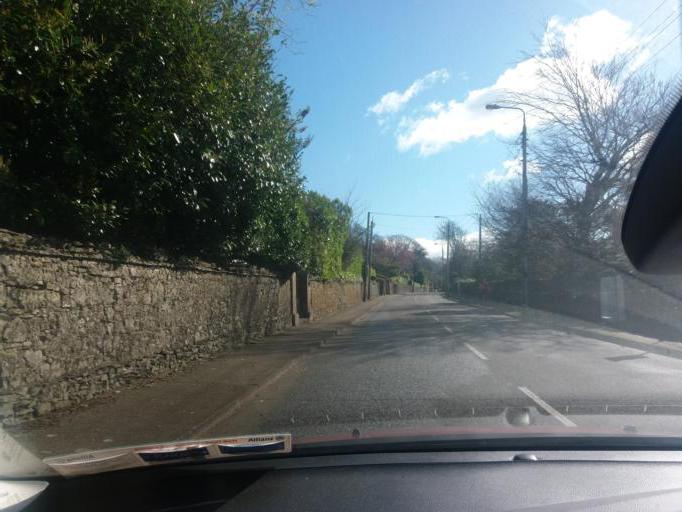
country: IE
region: Munster
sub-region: County Cork
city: Cobh
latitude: 51.8474
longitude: -8.3113
